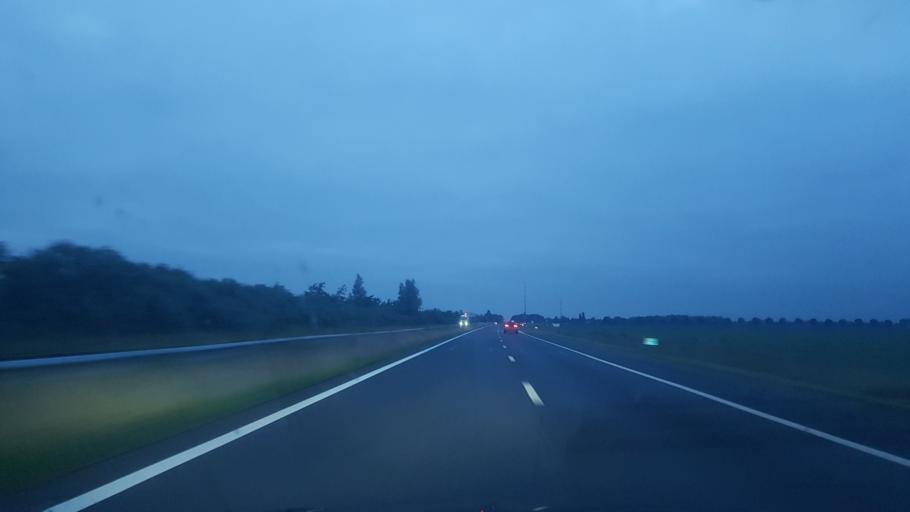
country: NL
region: Friesland
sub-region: Gemeente Boarnsterhim
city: Akkrum
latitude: 53.0669
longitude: 5.8349
